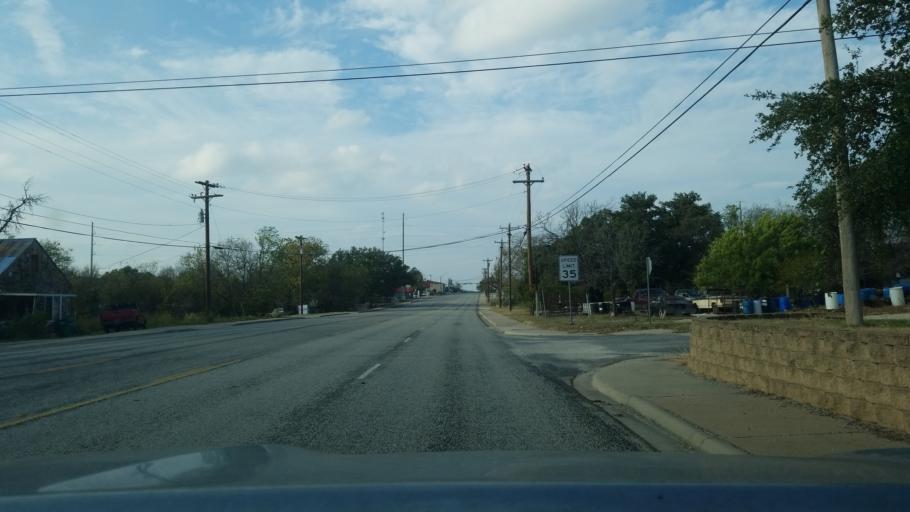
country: US
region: Texas
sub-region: Lampasas County
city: Lampasas
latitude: 31.2129
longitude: -98.3917
